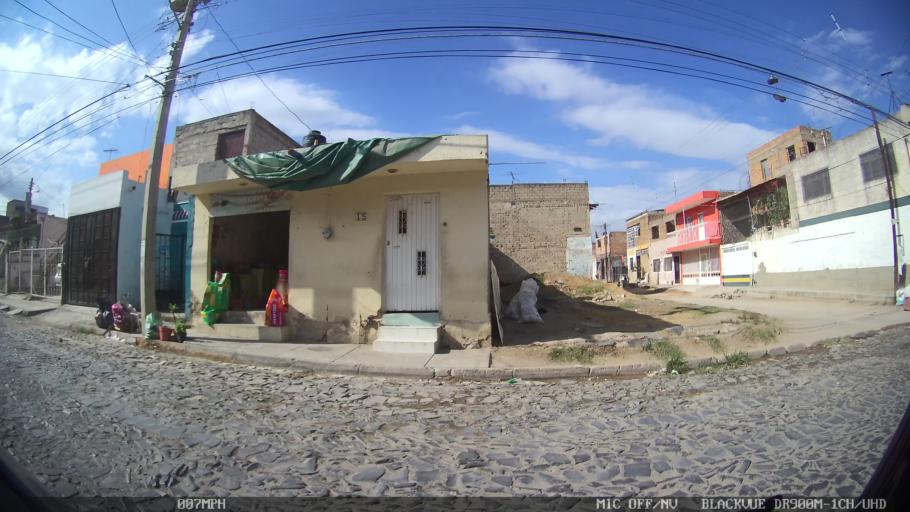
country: MX
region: Jalisco
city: Tonala
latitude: 20.6503
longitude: -103.2509
